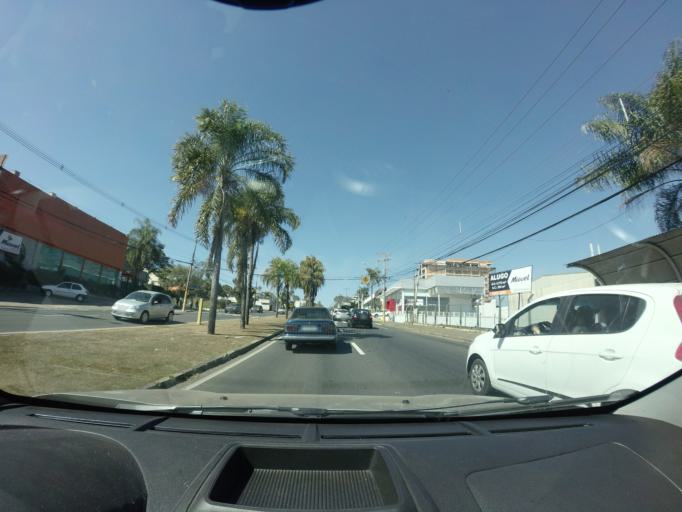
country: BR
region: Sao Paulo
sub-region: Piracicaba
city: Piracicaba
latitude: -22.7262
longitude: -47.6247
